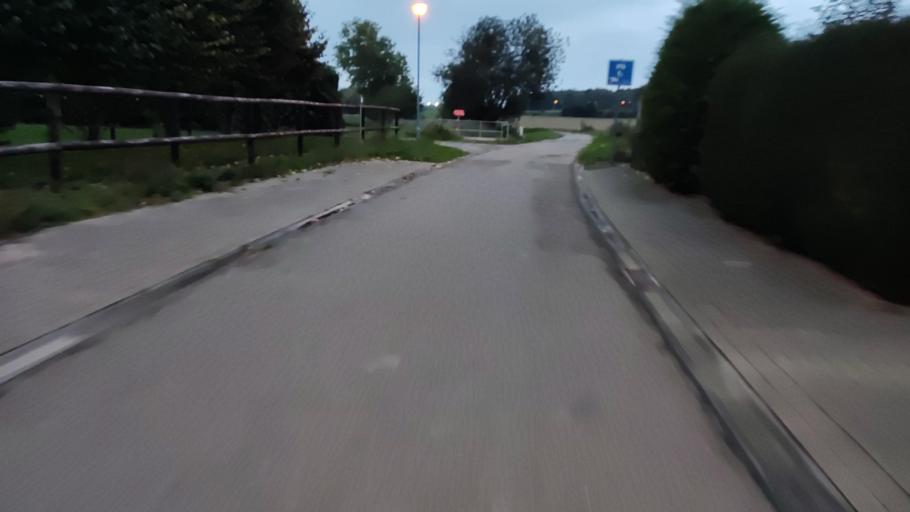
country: BE
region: Flanders
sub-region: Provincie Vlaams-Brabant
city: Hoegaarden
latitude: 50.7704
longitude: 4.9188
